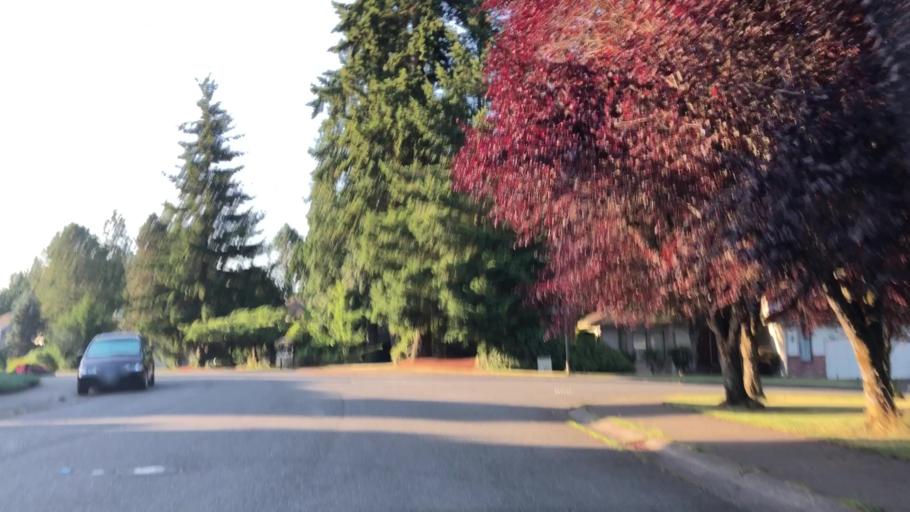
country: US
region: Washington
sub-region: King County
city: Cottage Lake
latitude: 47.7267
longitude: -122.1053
